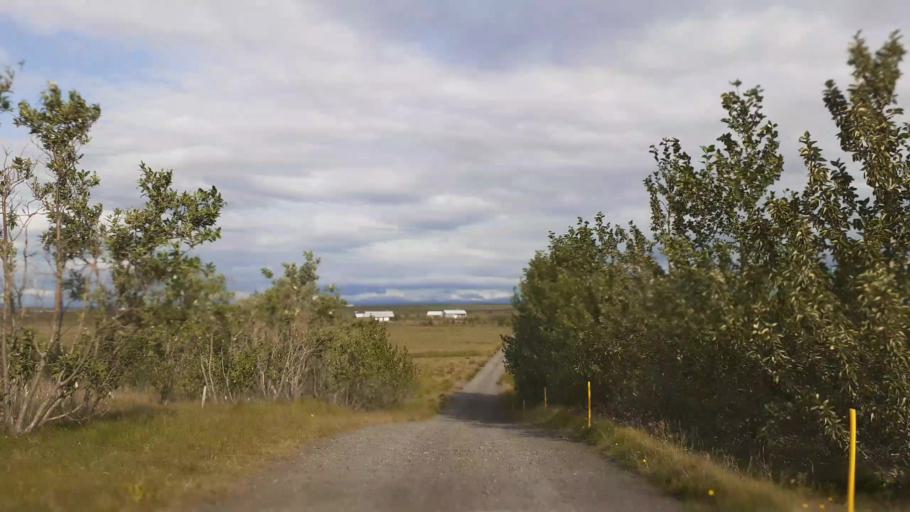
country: IS
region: South
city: Vestmannaeyjar
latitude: 63.7698
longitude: -20.2968
